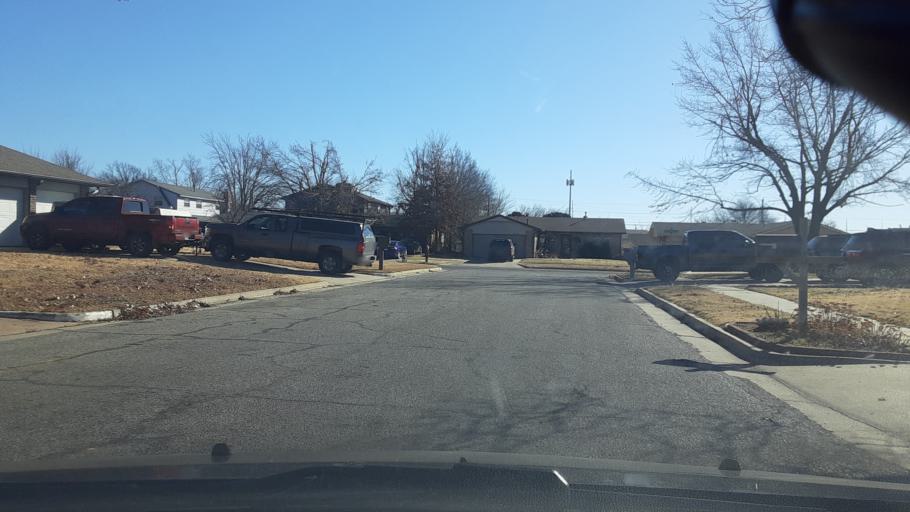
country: US
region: Oklahoma
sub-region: Kay County
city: Ponca City
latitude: 36.7285
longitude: -97.0880
